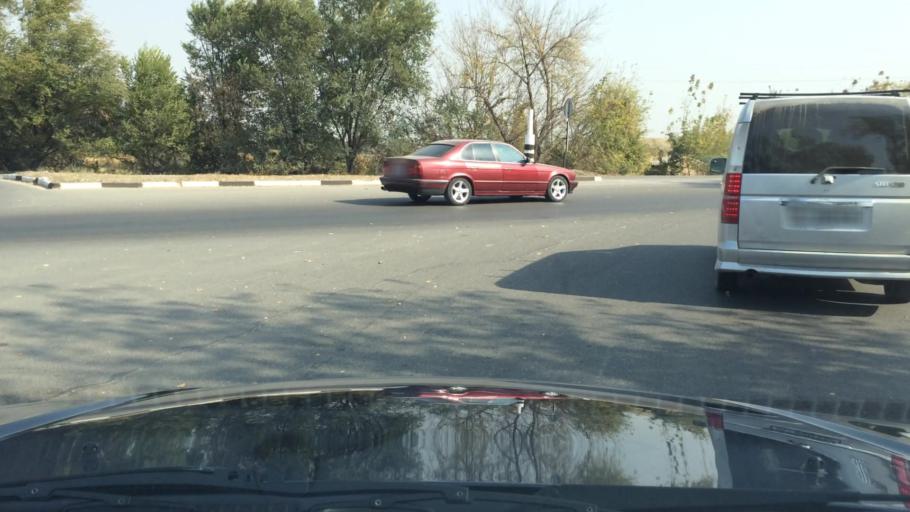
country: KG
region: Chuy
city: Lebedinovka
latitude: 42.9301
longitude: 74.6914
